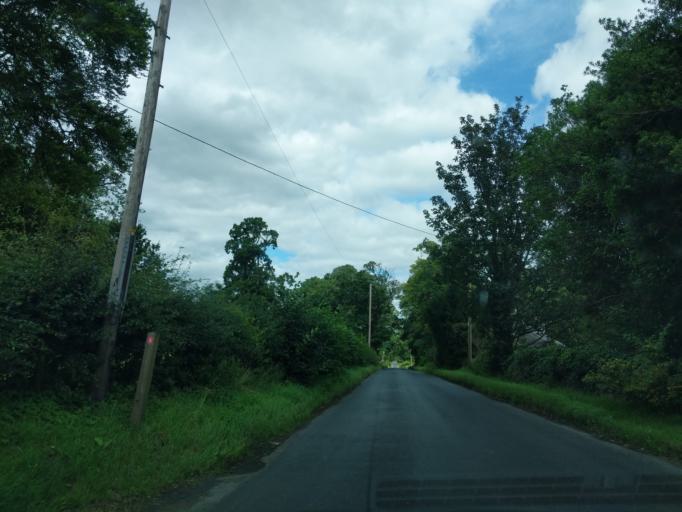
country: GB
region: Scotland
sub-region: The Scottish Borders
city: Peebles
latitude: 55.6180
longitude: -3.3067
